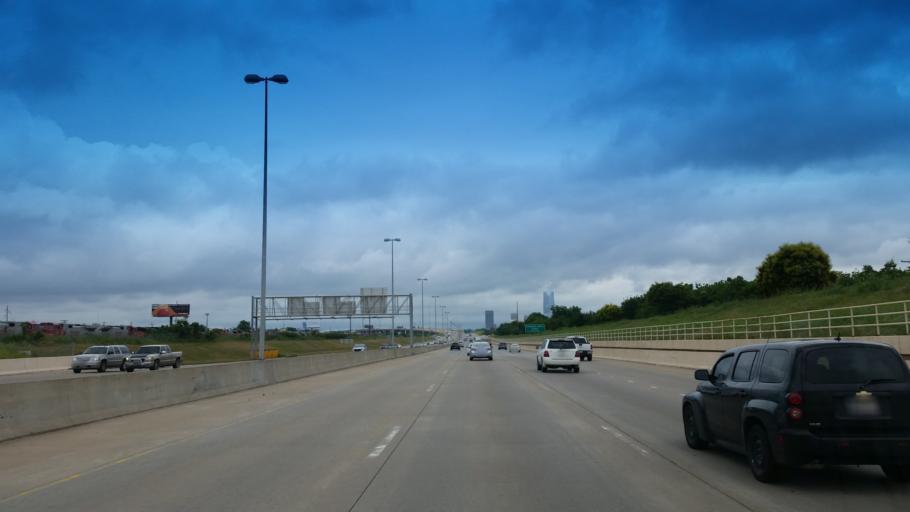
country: US
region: Oklahoma
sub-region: Oklahoma County
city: Oklahoma City
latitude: 35.5046
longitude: -97.5142
